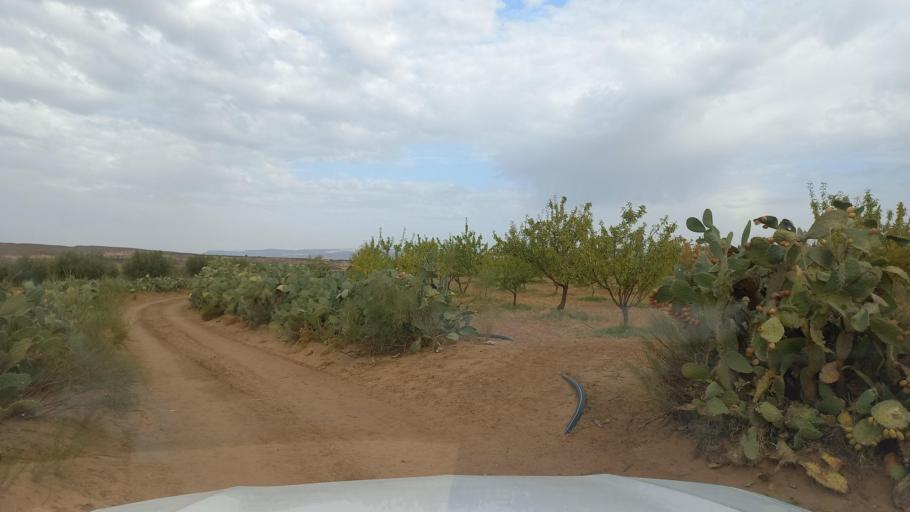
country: TN
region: Al Qasrayn
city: Kasserine
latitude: 35.1936
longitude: 9.0479
